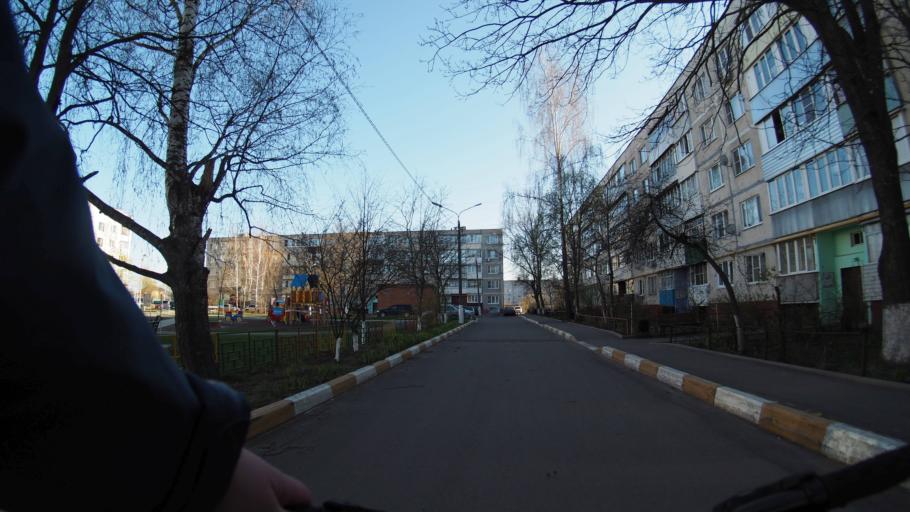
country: RU
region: Moskovskaya
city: Malyshevo
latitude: 55.5069
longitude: 38.3388
